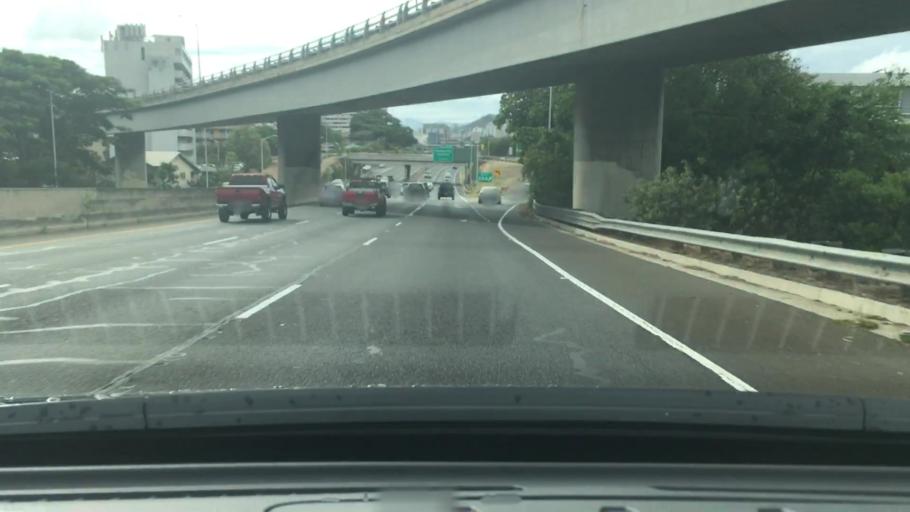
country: US
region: Hawaii
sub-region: Honolulu County
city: Honolulu
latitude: 21.2893
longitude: -157.8149
